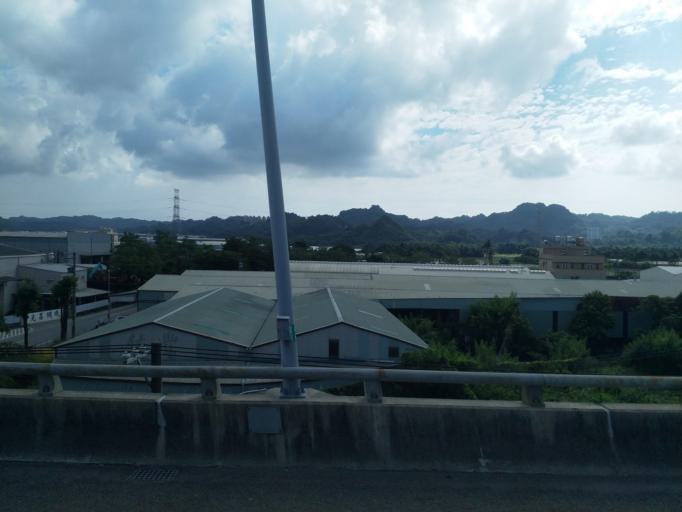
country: TW
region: Taiwan
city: Fengshan
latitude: 22.7380
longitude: 120.3616
